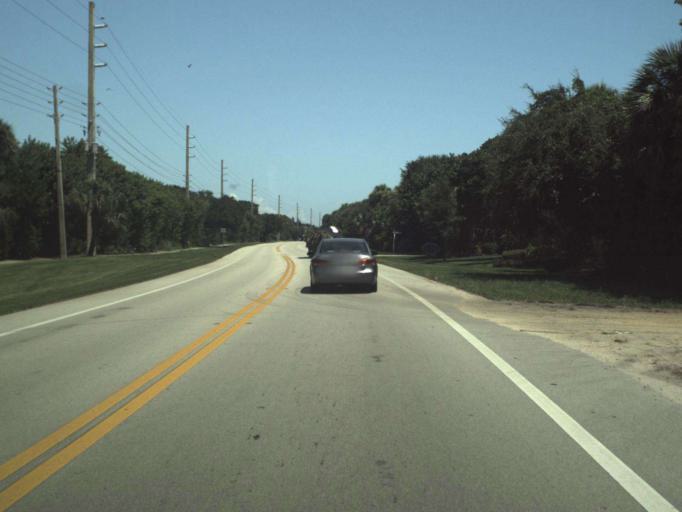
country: US
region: Florida
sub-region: Indian River County
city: South Beach
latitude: 27.6153
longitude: -80.3480
